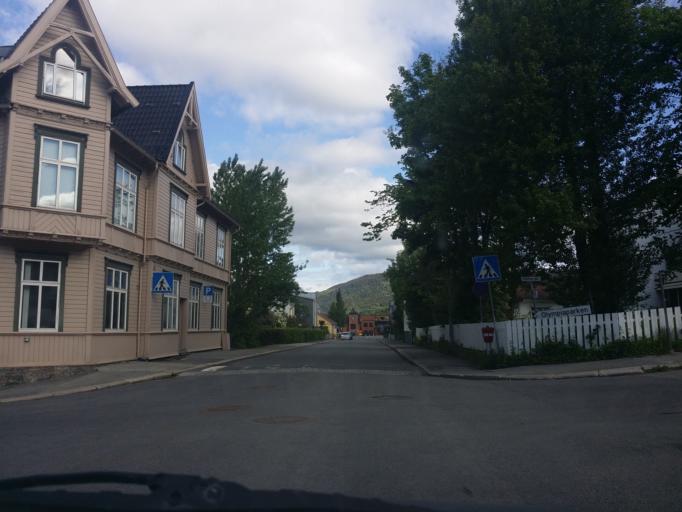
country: NO
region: Oppland
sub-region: Lillehammer
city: Lillehammer
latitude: 61.1144
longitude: 10.4696
